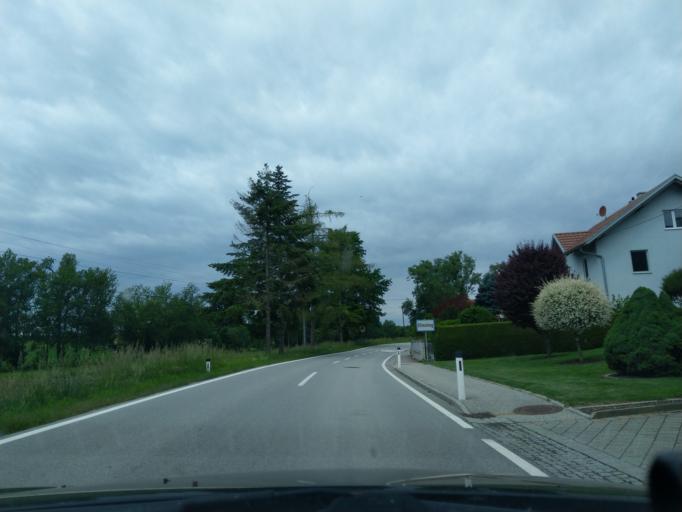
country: DE
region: Bavaria
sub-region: Lower Bavaria
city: Bad Fussing
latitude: 48.2806
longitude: 13.3663
